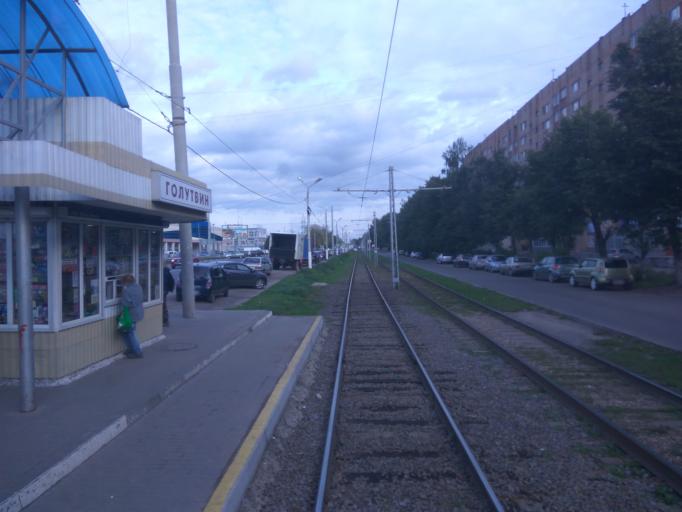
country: RU
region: Moskovskaya
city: Kolomna
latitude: 55.0837
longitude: 38.8041
